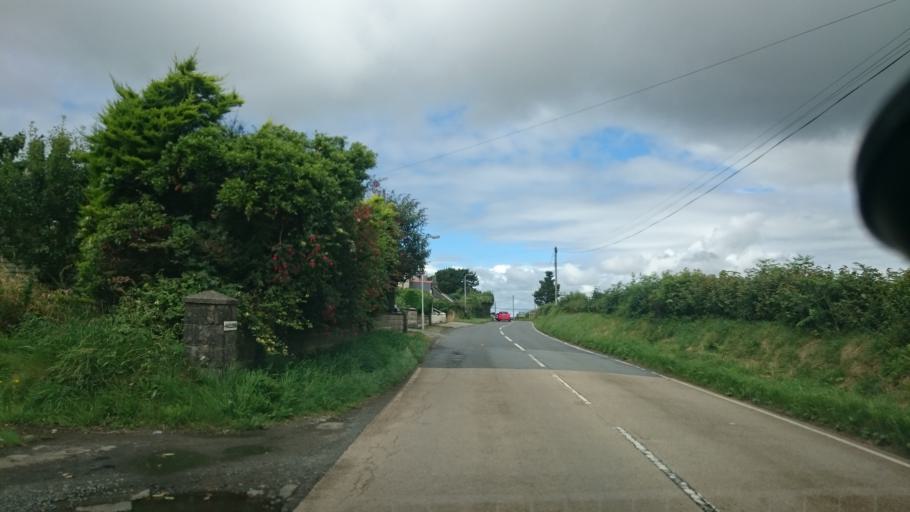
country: GB
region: Wales
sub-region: Pembrokeshire
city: Freystrop
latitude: 51.7524
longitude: -4.9534
